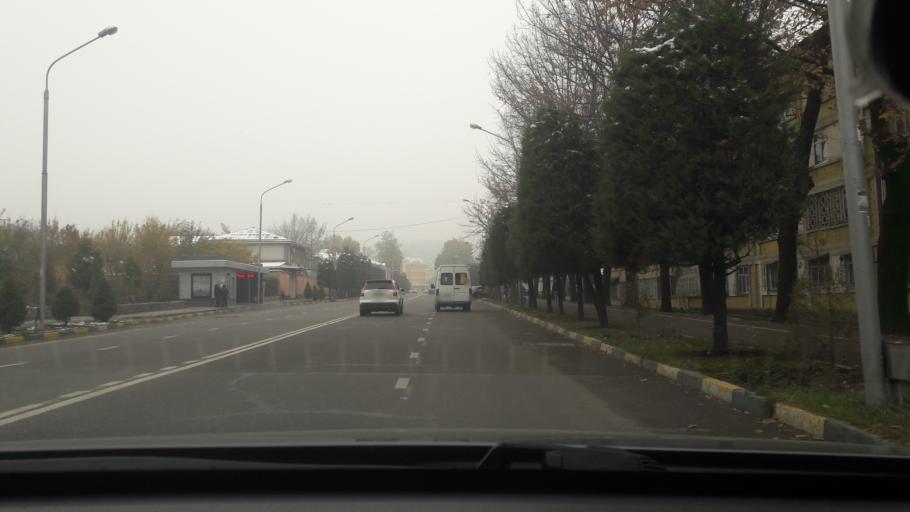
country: TJ
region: Dushanbe
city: Dushanbe
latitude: 38.5787
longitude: 68.7972
